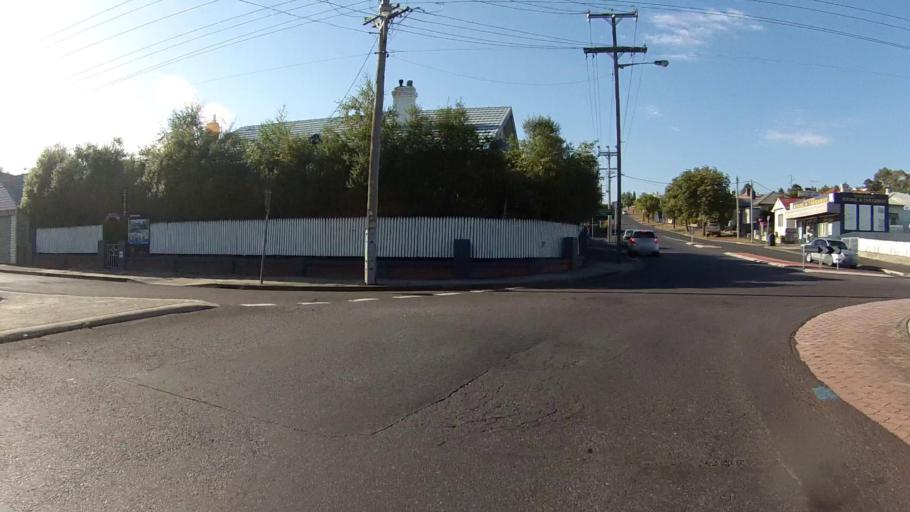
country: AU
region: Tasmania
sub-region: Derwent Valley
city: New Norfolk
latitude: -42.7802
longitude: 147.0575
